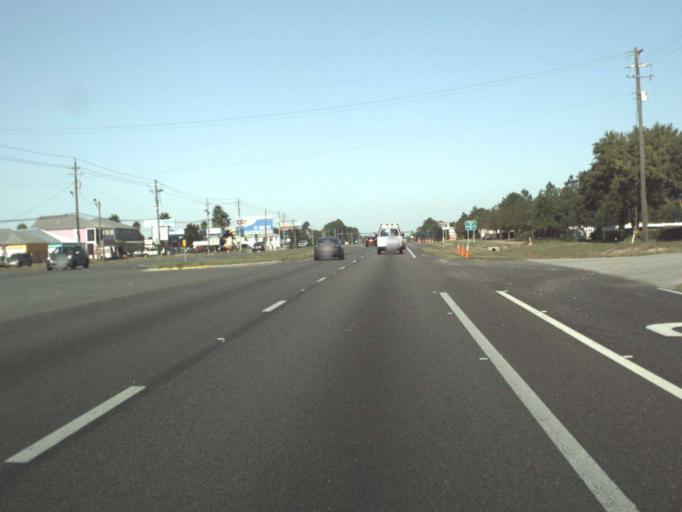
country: US
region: Florida
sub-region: Bay County
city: Panama City Beach
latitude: 30.2077
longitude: -85.8442
